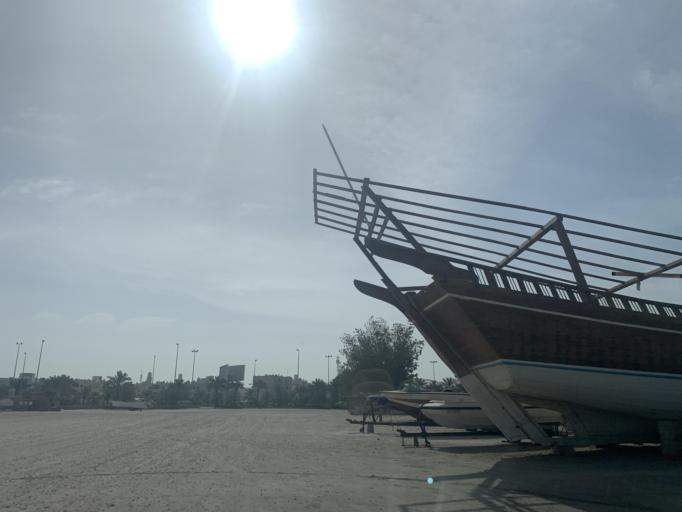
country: BH
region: Muharraq
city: Al Muharraq
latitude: 26.2595
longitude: 50.6015
